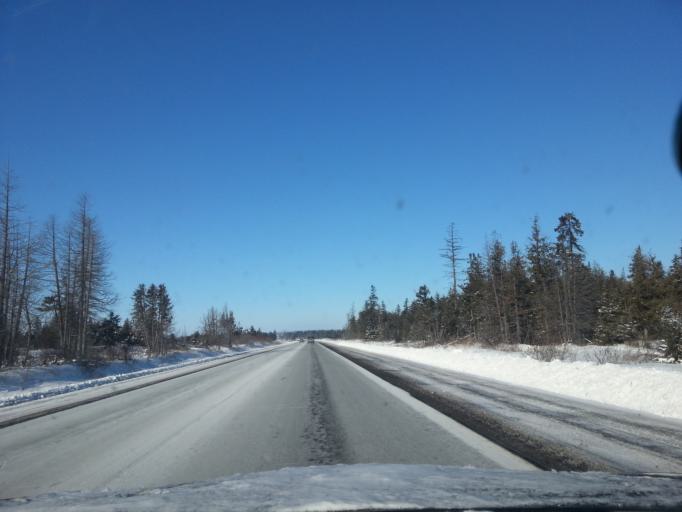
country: CA
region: Ontario
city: Arnprior
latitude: 45.3449
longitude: -76.1976
